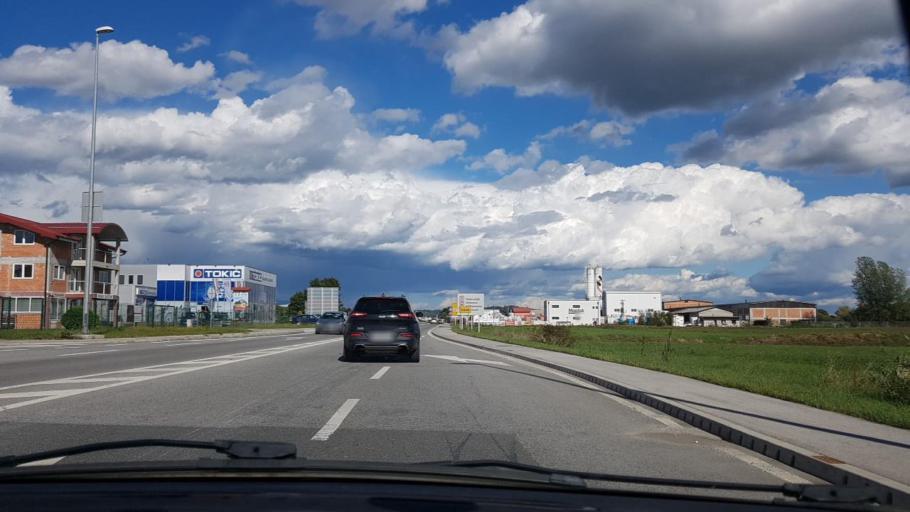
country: HR
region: Krapinsko-Zagorska
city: Oroslavje
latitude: 46.0100
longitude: 15.8785
